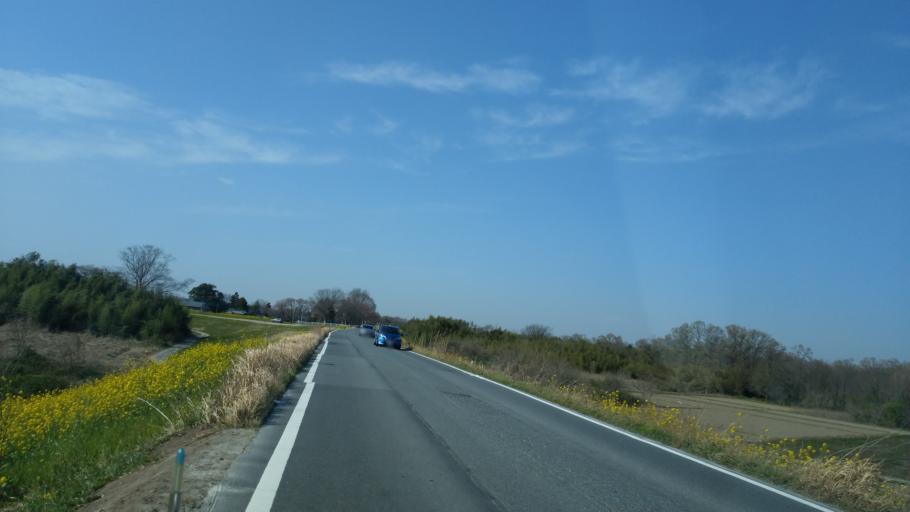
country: JP
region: Saitama
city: Okegawa
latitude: 35.9510
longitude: 139.5324
